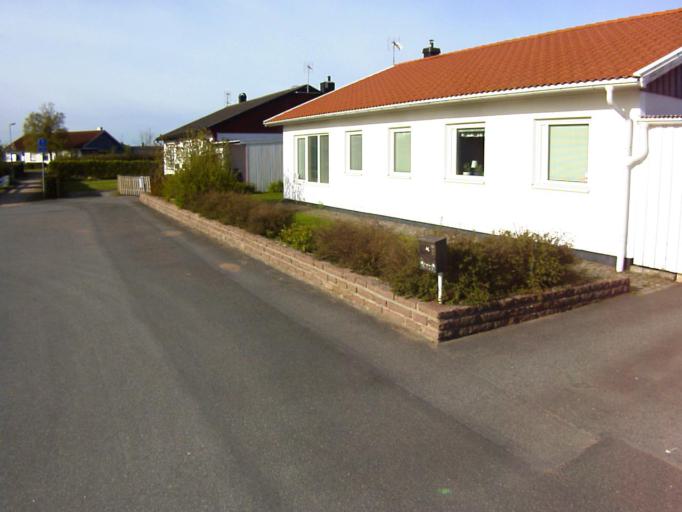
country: SE
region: Skane
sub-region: Kristianstads Kommun
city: Kristianstad
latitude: 56.0112
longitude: 14.1458
